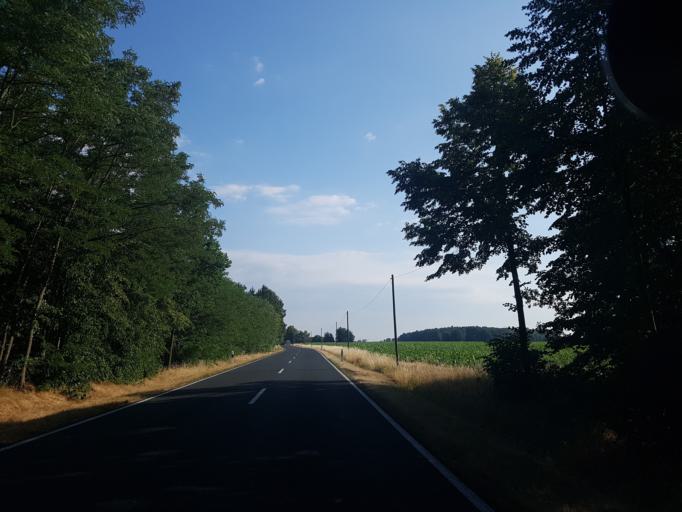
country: DE
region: Saxony-Anhalt
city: Seyda
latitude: 51.9267
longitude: 12.9138
